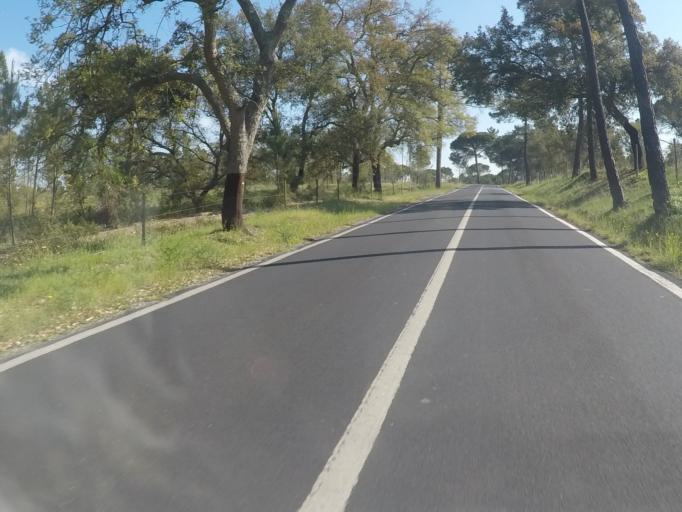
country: PT
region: Setubal
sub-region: Seixal
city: Arrentela
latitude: 38.5427
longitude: -9.1116
